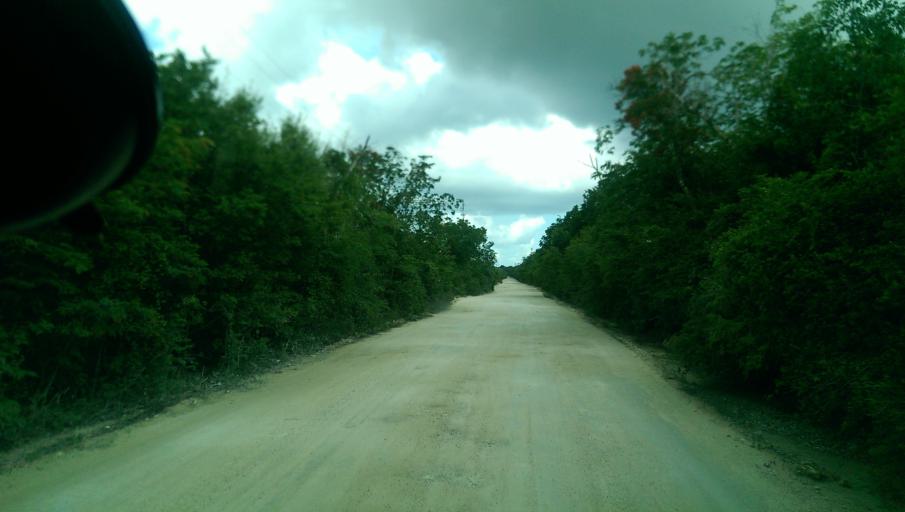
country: MX
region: Quintana Roo
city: Playa del Carmen
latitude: 20.5908
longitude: -87.1413
